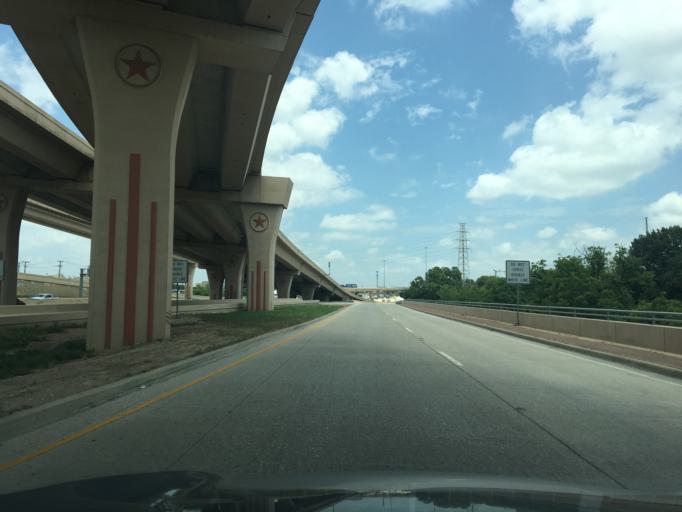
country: US
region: Texas
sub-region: Dallas County
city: Richardson
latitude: 32.9265
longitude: -96.7614
